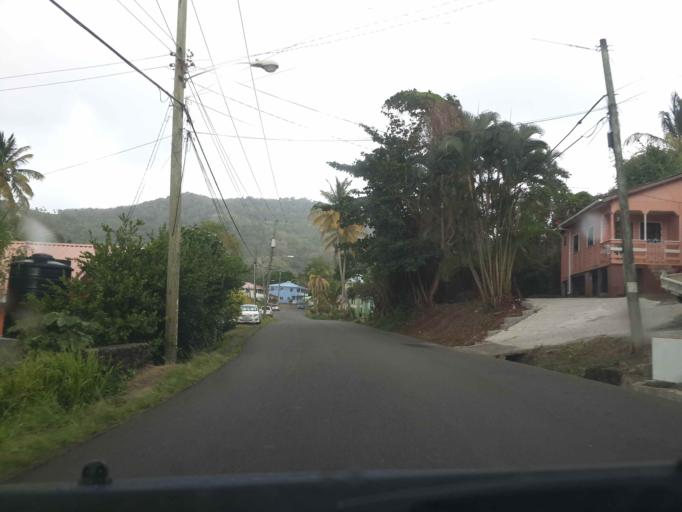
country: LC
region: Castries Quarter
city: Bisee
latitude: 14.0381
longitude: -60.9526
